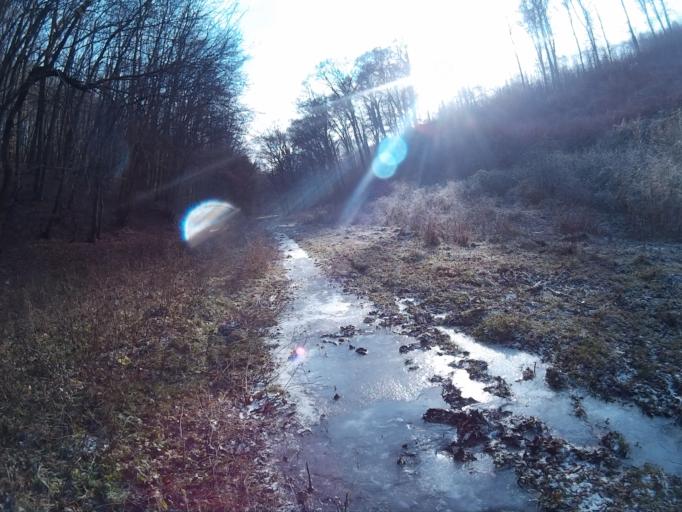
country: HU
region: Komarom-Esztergom
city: Tatabanya
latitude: 47.5031
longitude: 18.4117
